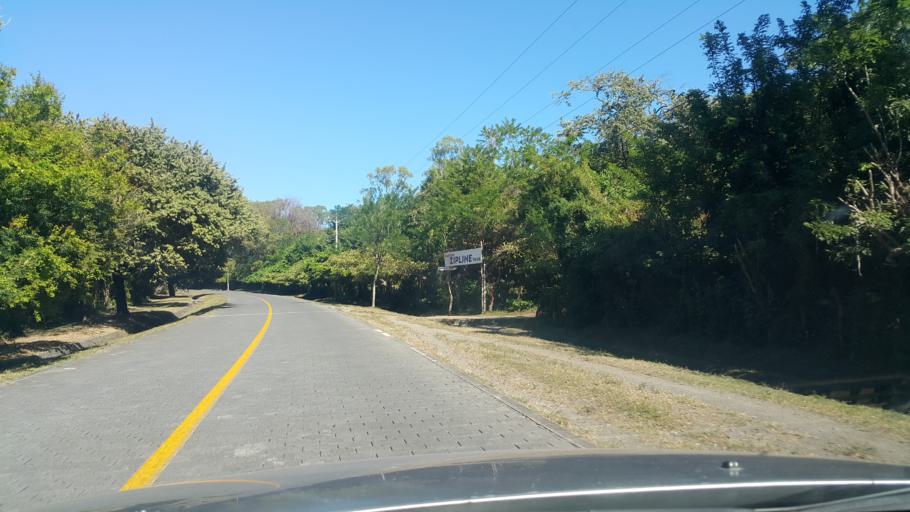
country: NI
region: Rivas
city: Moyogalpa
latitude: 11.4864
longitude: -85.6342
